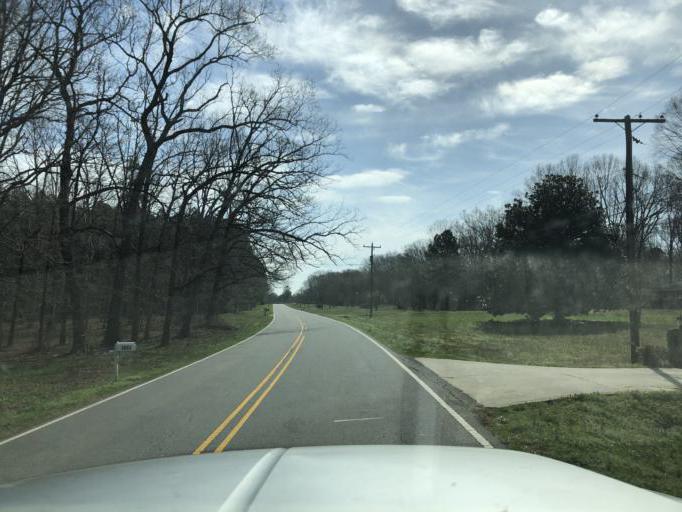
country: US
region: North Carolina
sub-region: Cleveland County
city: Shelby
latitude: 35.3804
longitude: -81.6155
